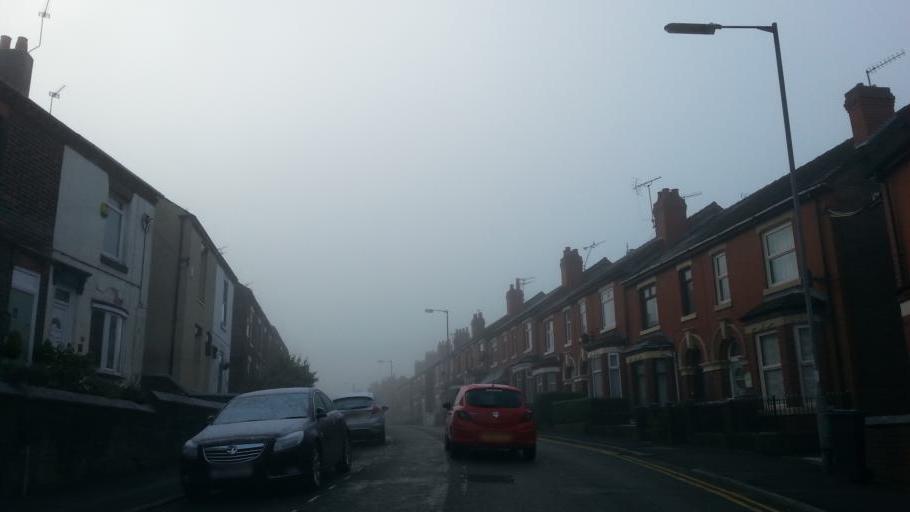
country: GB
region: England
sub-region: Staffordshire
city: Biddulph
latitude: 53.1133
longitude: -2.1775
